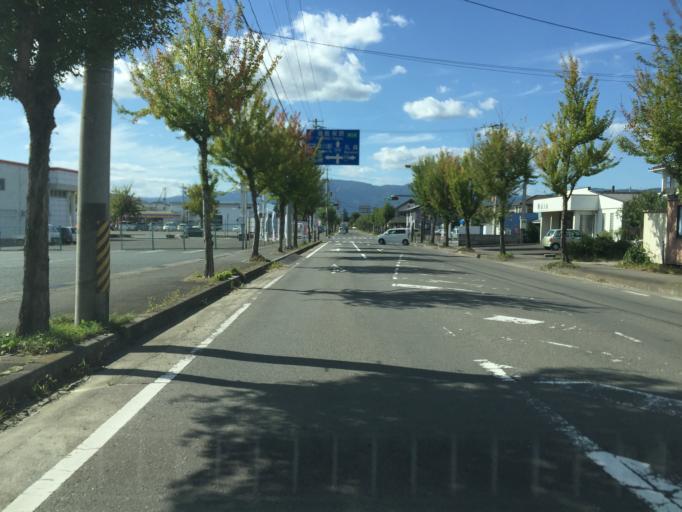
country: JP
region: Fukushima
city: Yanagawamachi-saiwaicho
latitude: 37.8506
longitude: 140.6053
